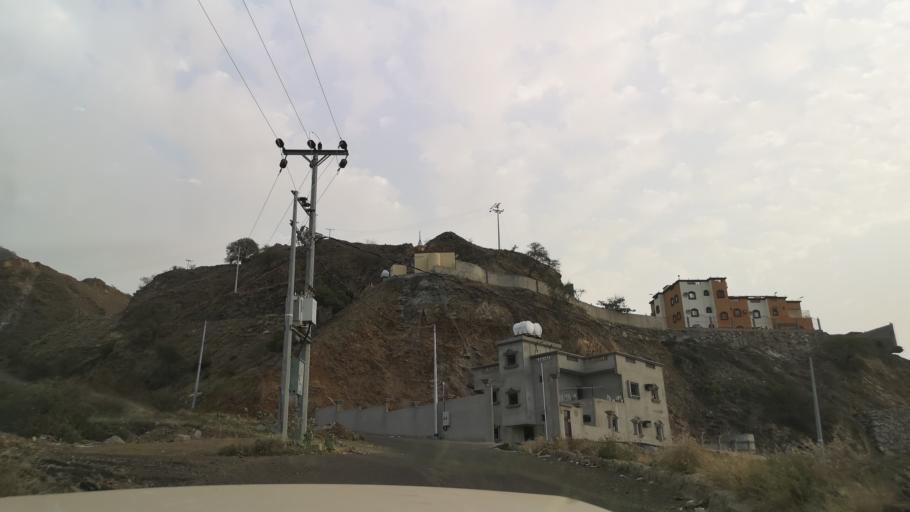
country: YE
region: Sa'dah
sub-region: Monabbih
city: Suq al Khamis
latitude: 17.3281
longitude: 43.1448
